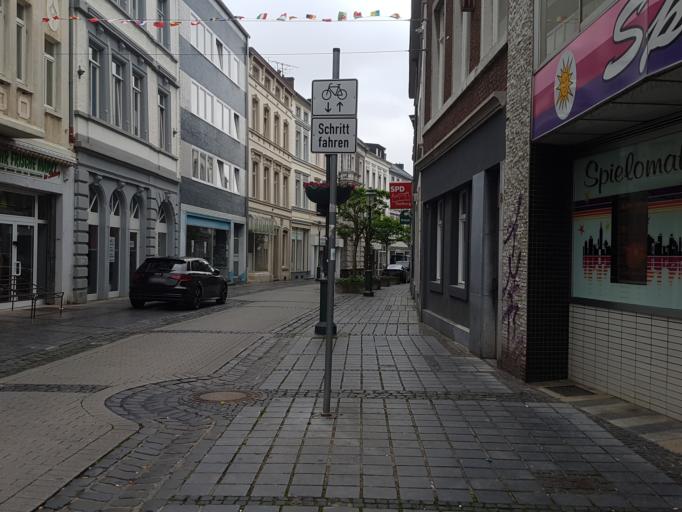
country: DE
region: North Rhine-Westphalia
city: Stolberg
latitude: 50.7663
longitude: 6.2317
